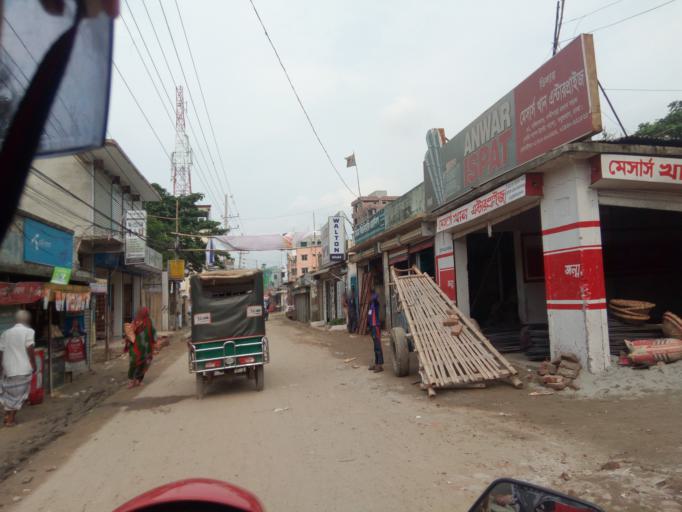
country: BD
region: Dhaka
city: Paltan
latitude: 23.7447
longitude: 90.4473
